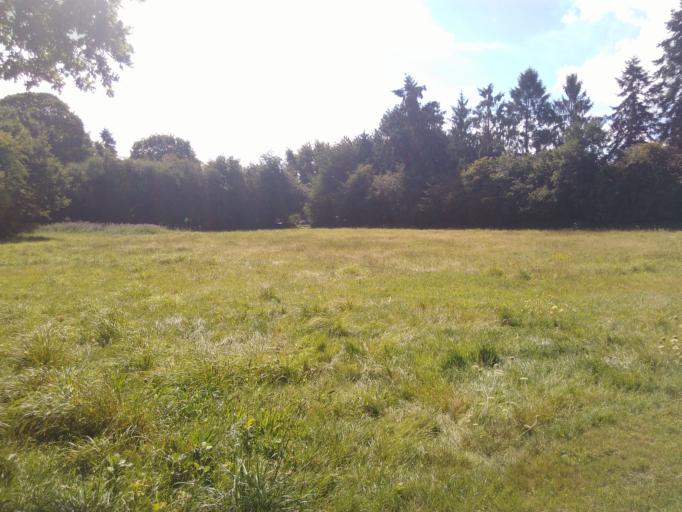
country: FR
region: Brittany
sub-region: Departement d'Ille-et-Vilaine
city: Saint-Sulpice-la-Foret
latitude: 48.2198
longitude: -1.5804
